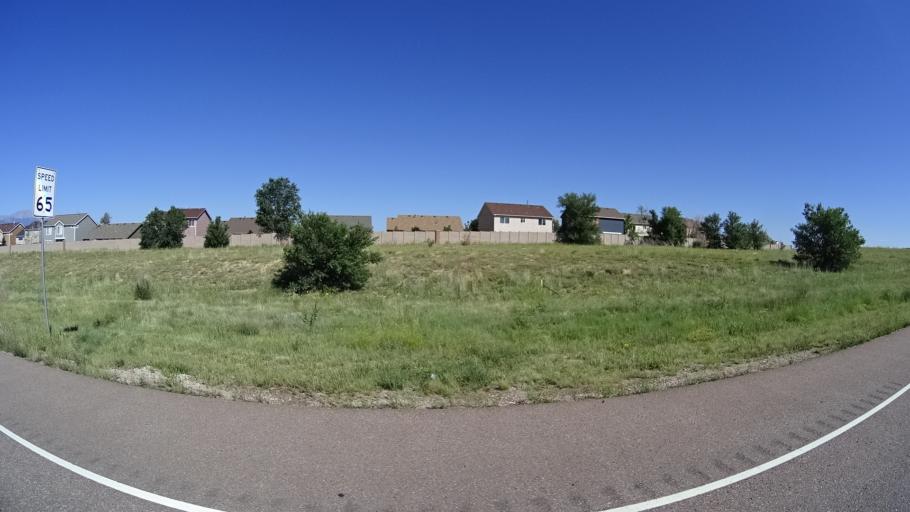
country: US
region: Colorado
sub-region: El Paso County
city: Cimarron Hills
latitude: 38.8625
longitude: -104.6659
